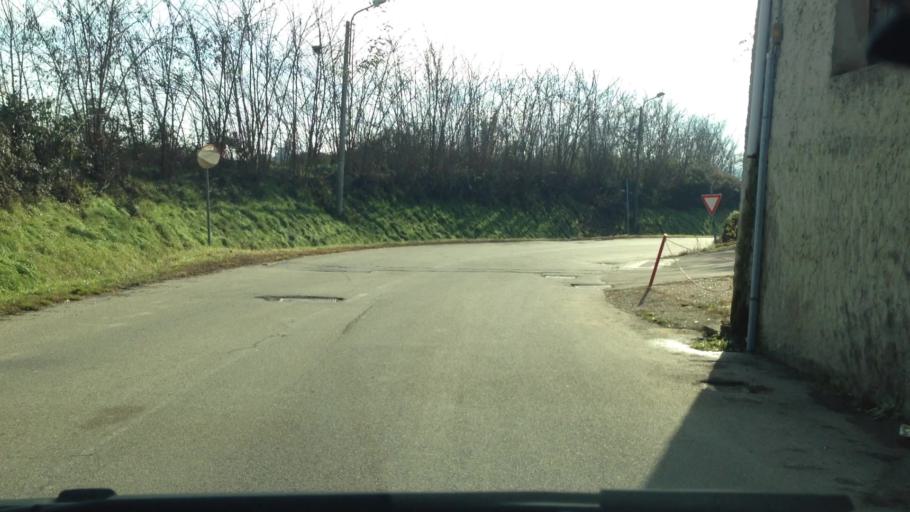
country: IT
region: Piedmont
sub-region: Provincia di Alessandria
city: Quattordio
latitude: 44.8968
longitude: 8.4071
